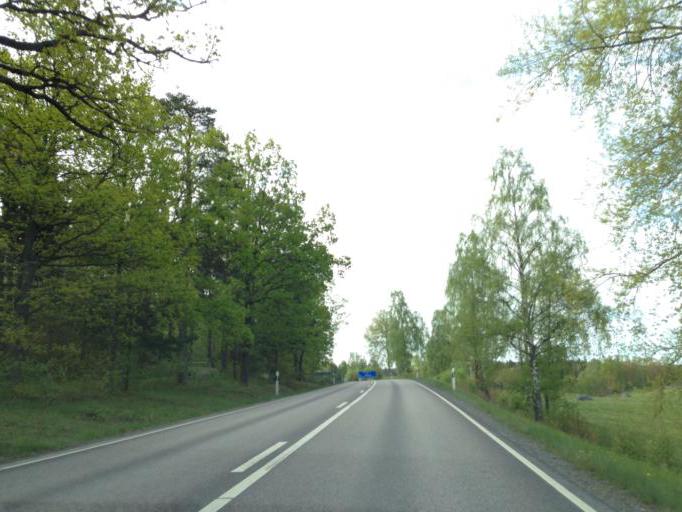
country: SE
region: Soedermanland
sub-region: Flens Kommun
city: Malmkoping
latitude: 59.0712
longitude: 16.8172
